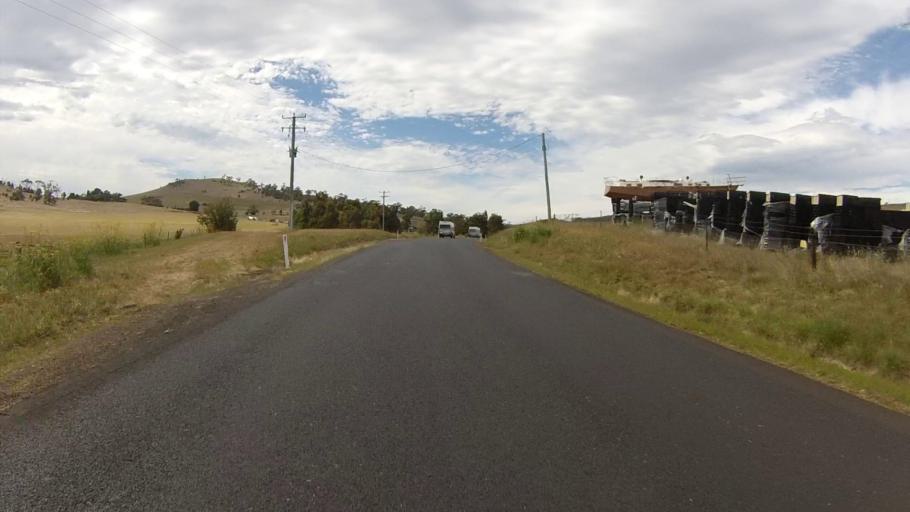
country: AU
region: Tasmania
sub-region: Brighton
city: Old Beach
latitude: -42.7035
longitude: 147.3107
